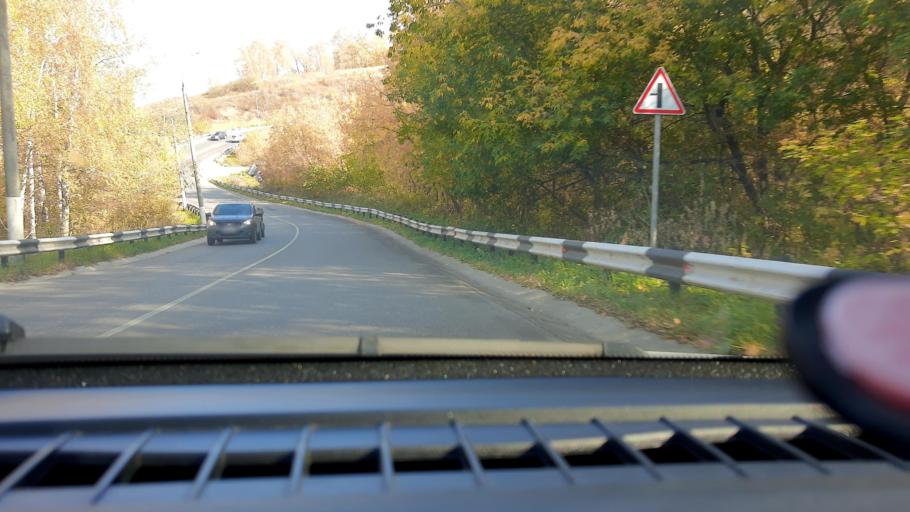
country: RU
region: Nizjnij Novgorod
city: Kstovo
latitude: 56.1562
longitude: 44.2448
